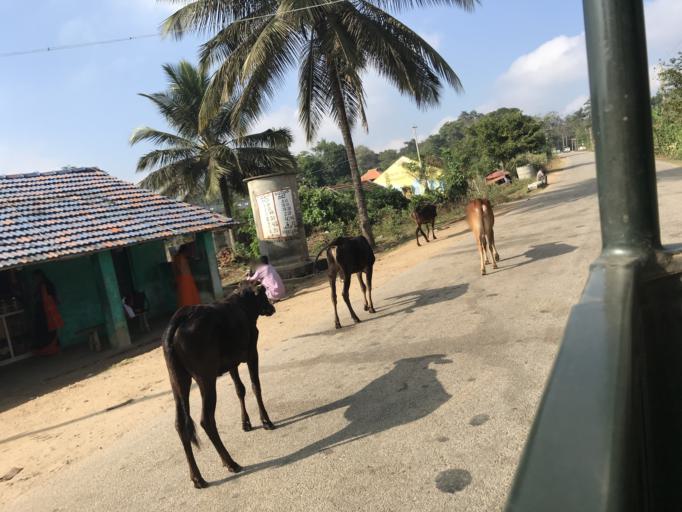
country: IN
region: Karnataka
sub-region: Mysore
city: Heggadadevankote
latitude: 11.9452
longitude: 76.2390
